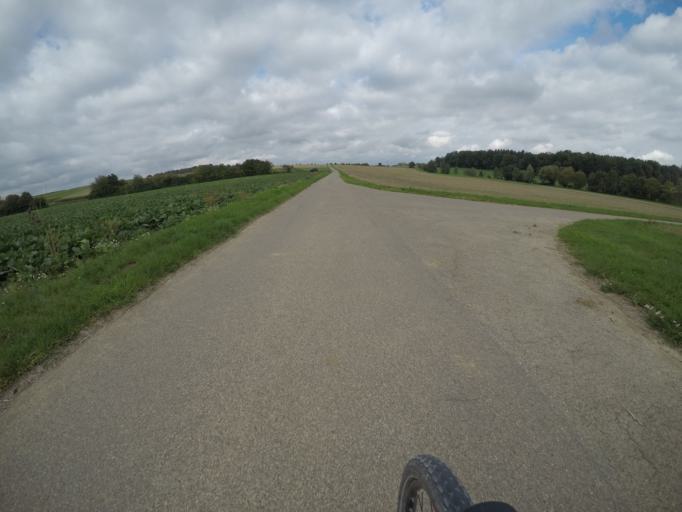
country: DE
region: Baden-Wuerttemberg
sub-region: Regierungsbezirk Stuttgart
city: Renningen
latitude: 48.7427
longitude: 8.9177
